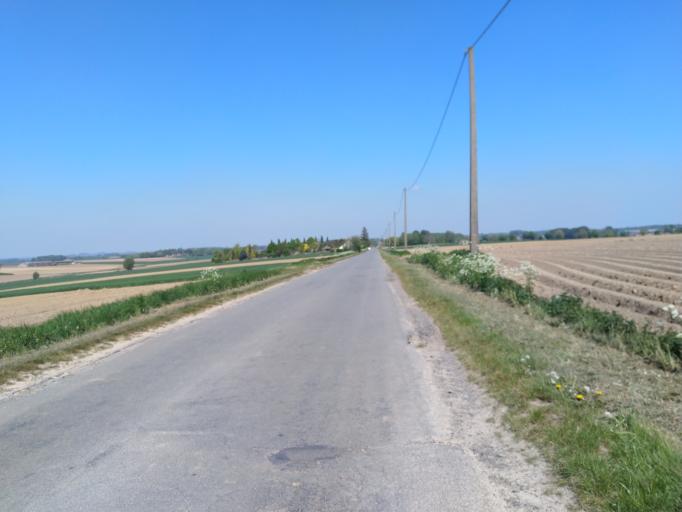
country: BE
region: Wallonia
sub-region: Province du Hainaut
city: Enghien
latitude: 50.6525
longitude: 4.0318
